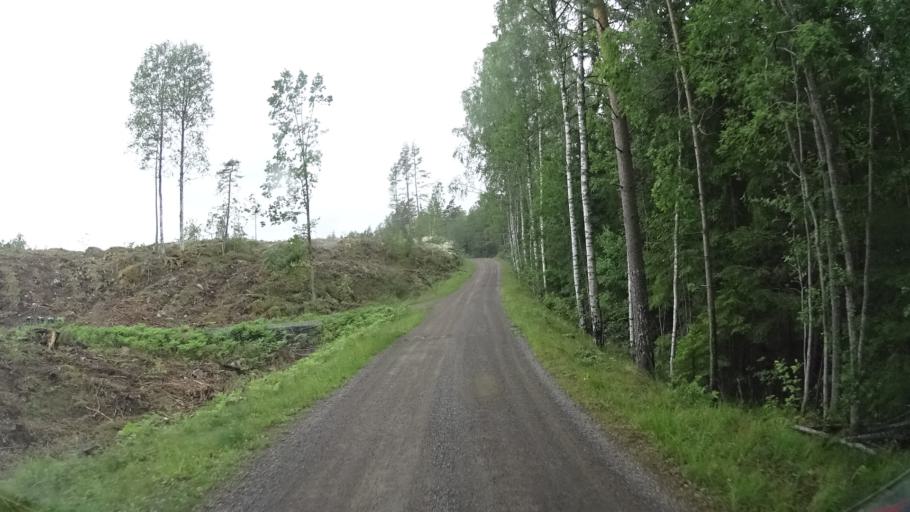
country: SE
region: Kalmar
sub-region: Oskarshamns Kommun
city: Oskarshamn
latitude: 57.3730
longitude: 16.2338
